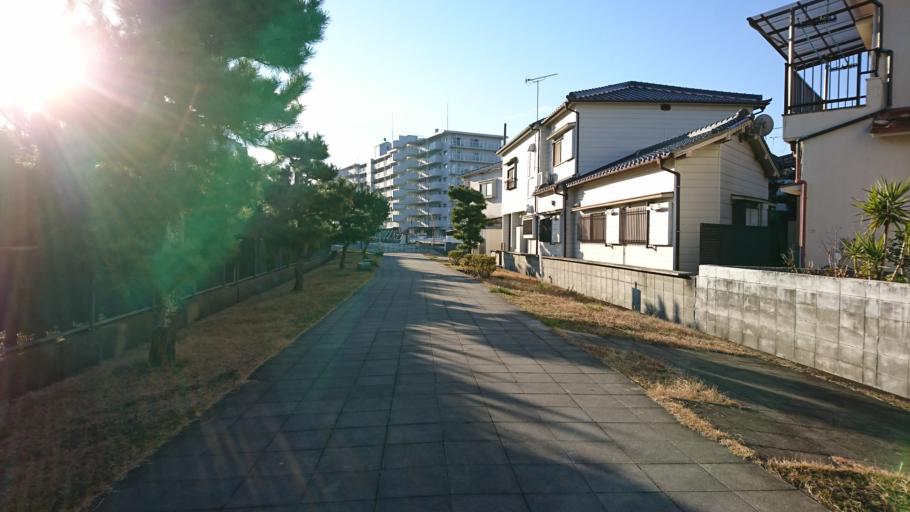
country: JP
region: Hyogo
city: Kakogawacho-honmachi
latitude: 34.7515
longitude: 134.8375
